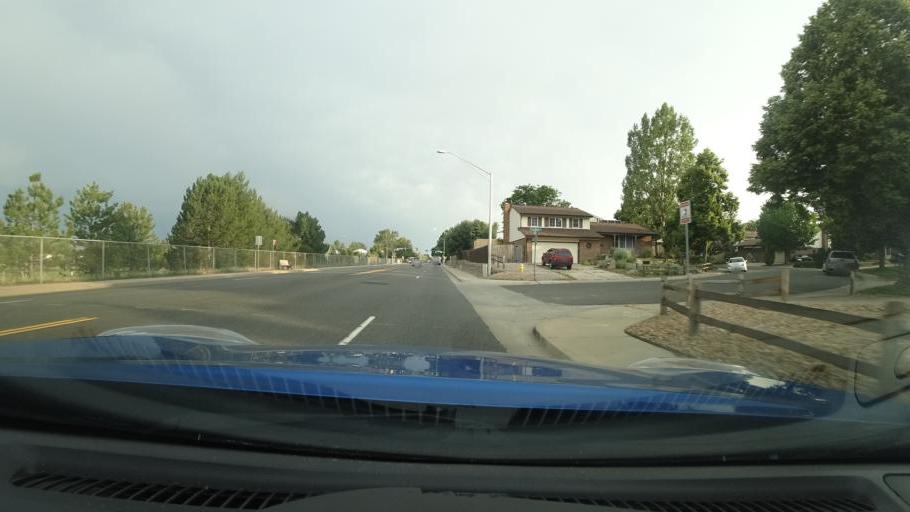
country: US
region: Colorado
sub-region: Adams County
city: Aurora
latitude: 39.6909
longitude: -104.8193
